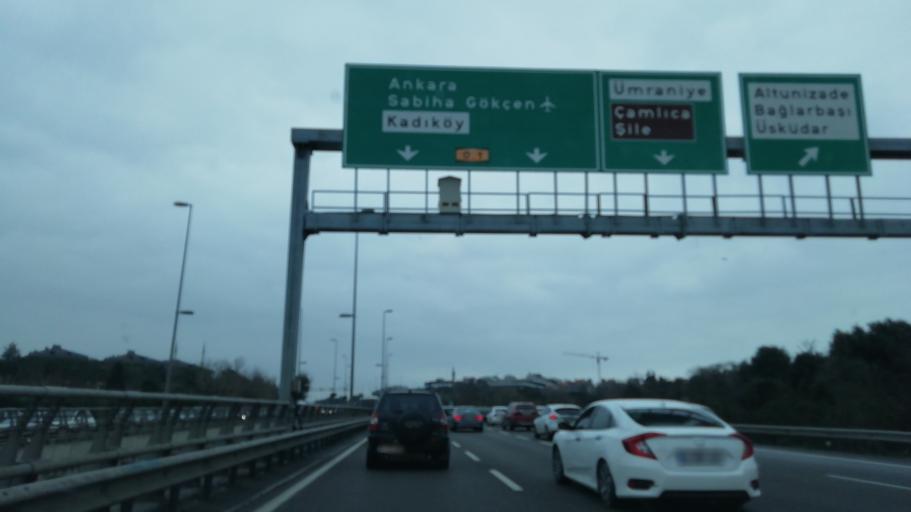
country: TR
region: Istanbul
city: UEskuedar
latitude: 41.0295
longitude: 29.0456
